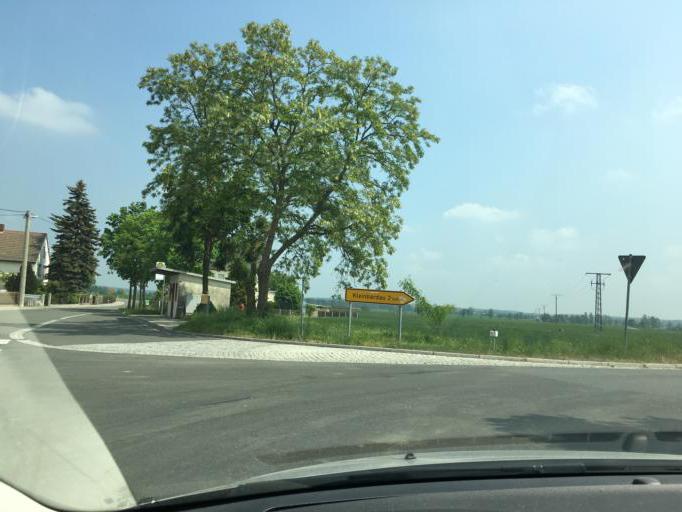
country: DE
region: Saxony
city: Grossbardau
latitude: 51.1849
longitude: 12.6651
